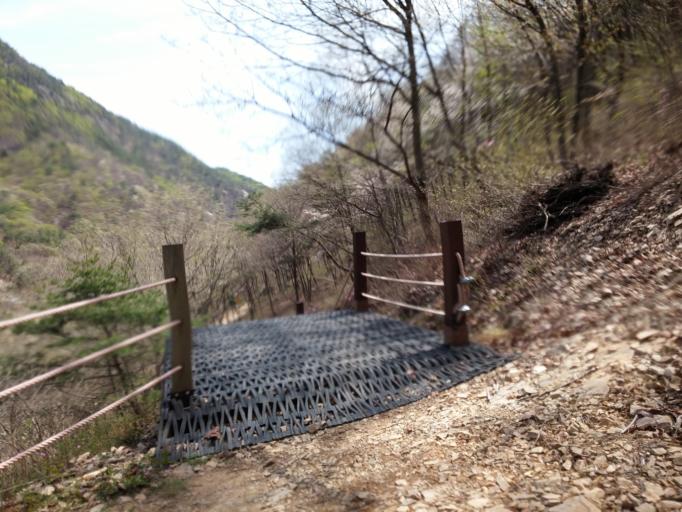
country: KR
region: Chungcheongbuk-do
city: Okcheon
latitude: 36.2345
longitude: 127.5603
